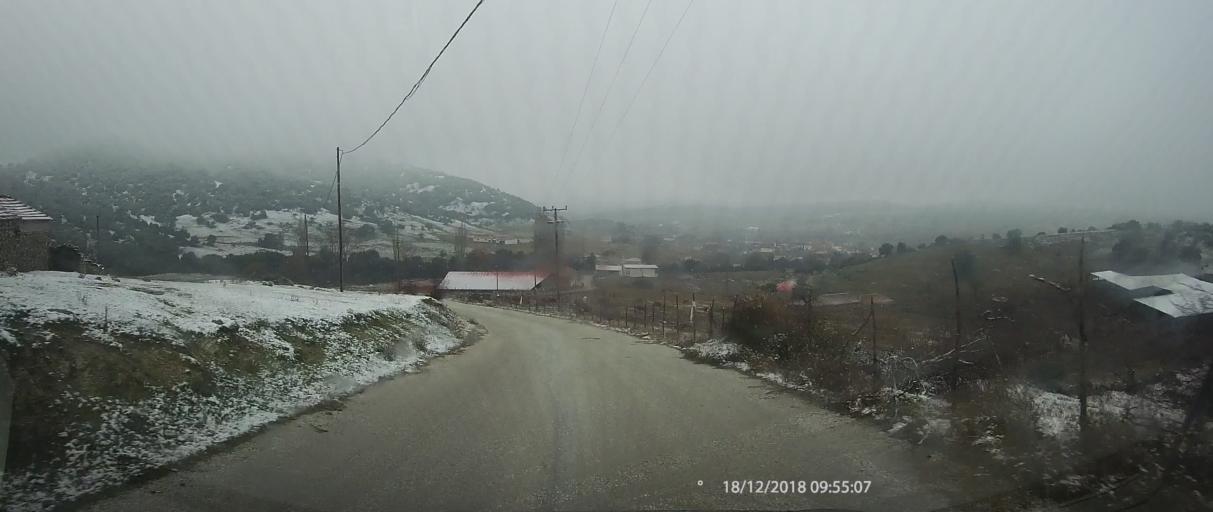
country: GR
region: Thessaly
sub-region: Nomos Larisis
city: Livadi
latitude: 40.0266
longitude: 22.2506
